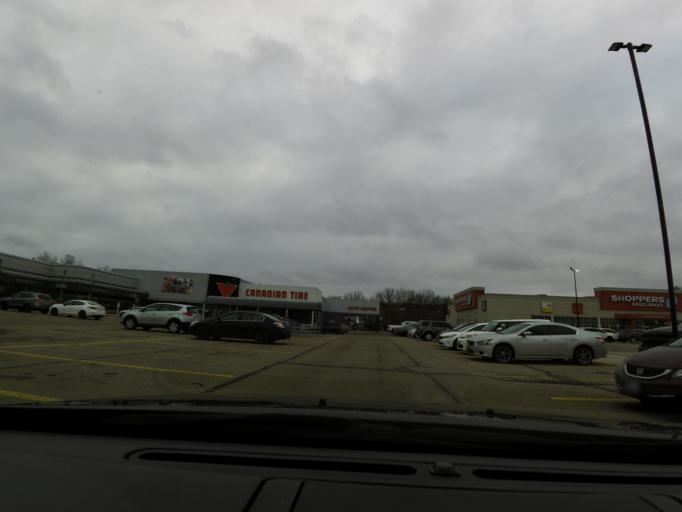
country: CA
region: Ontario
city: Ancaster
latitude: 43.2579
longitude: -79.9421
